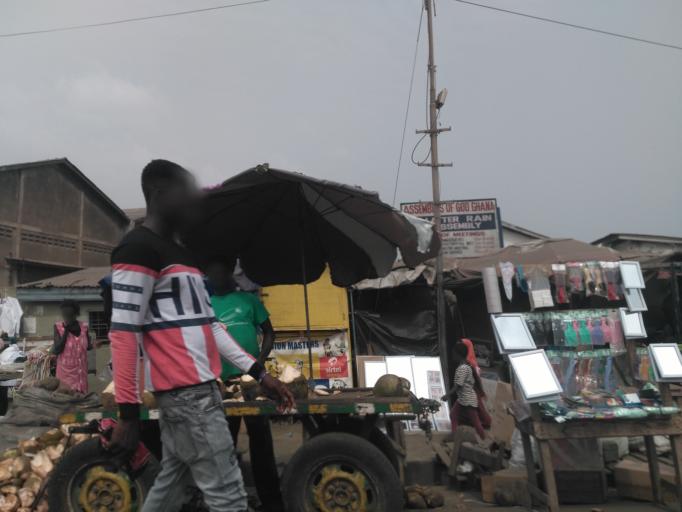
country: GH
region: Greater Accra
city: Accra
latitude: 5.5479
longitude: -0.2179
